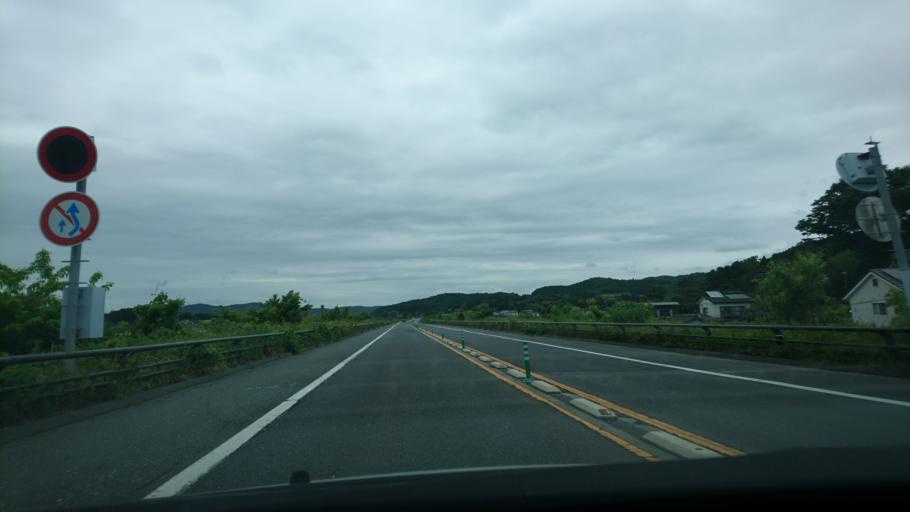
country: JP
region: Miyagi
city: Wakuya
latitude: 38.5805
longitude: 141.2740
